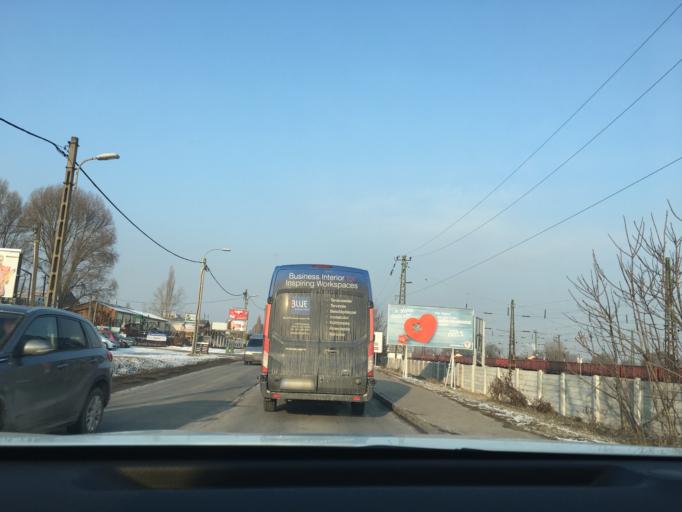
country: HU
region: Budapest
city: Budapest X. keruelet
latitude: 47.4876
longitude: 19.1778
